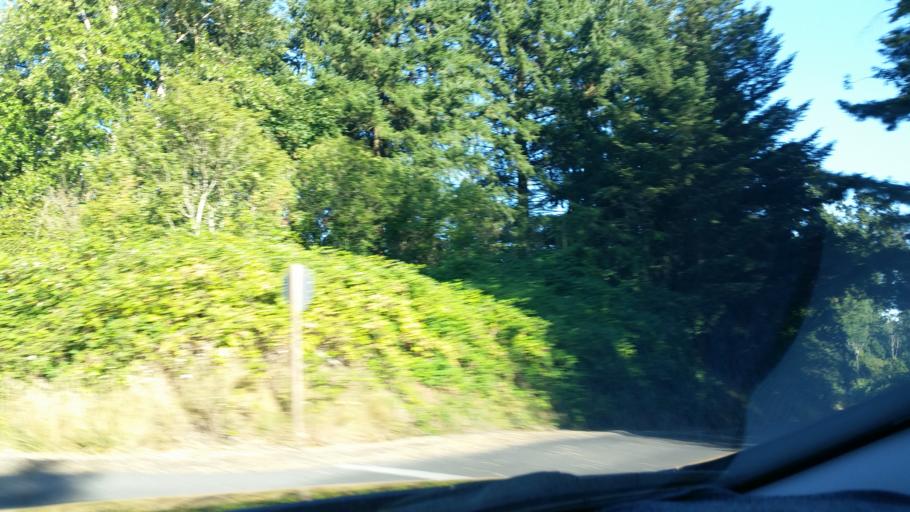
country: US
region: Oregon
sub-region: Marion County
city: Hubbard
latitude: 45.2293
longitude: -122.8566
